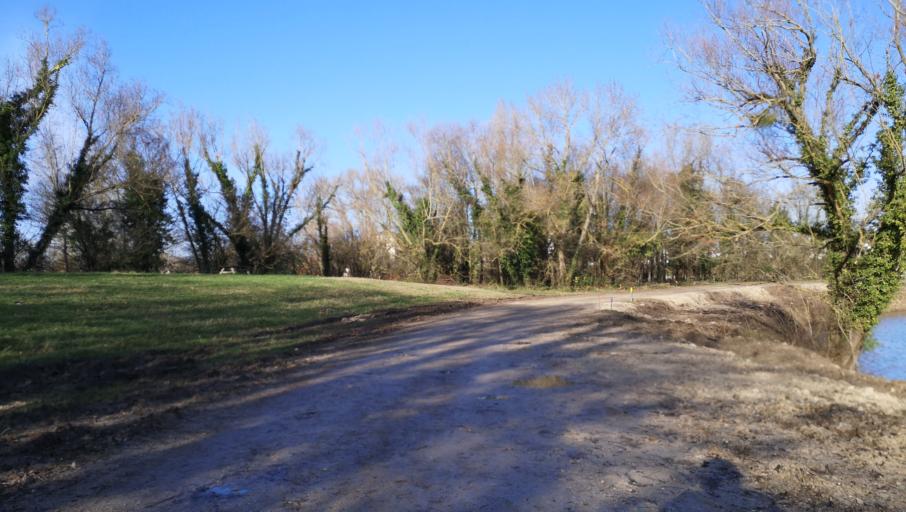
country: FR
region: Centre
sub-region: Departement du Loiret
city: Saint-Jean-le-Blanc
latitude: 47.8971
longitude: 1.9357
